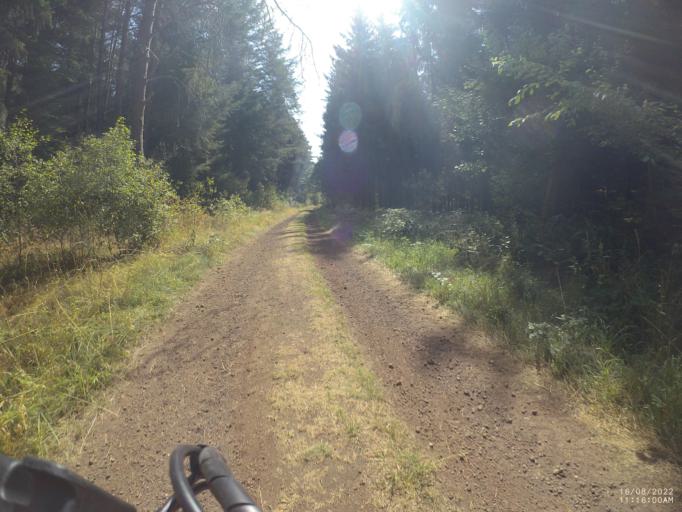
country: DE
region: Rheinland-Pfalz
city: Birgel
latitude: 50.3164
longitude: 6.6396
